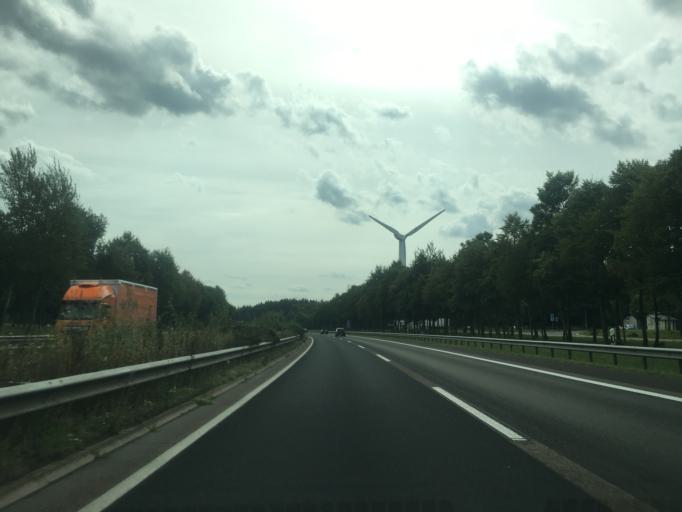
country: DE
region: Rheinland-Pfalz
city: Hungenroth
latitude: 50.1347
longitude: 7.5922
